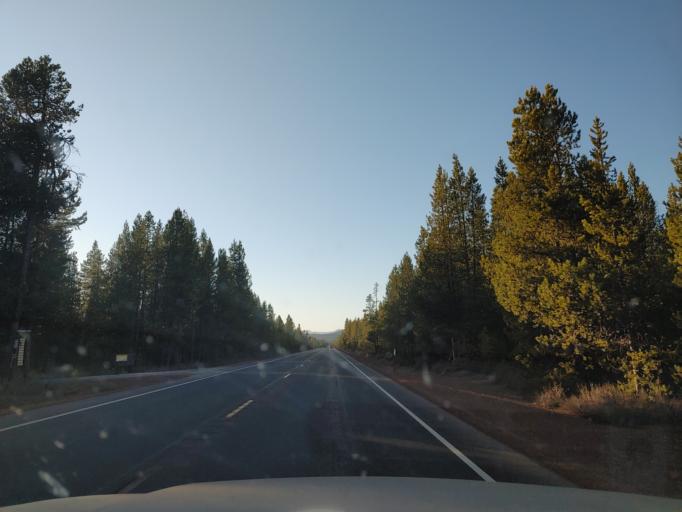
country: US
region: Oregon
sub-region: Deschutes County
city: La Pine
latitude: 43.3965
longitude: -121.8171
